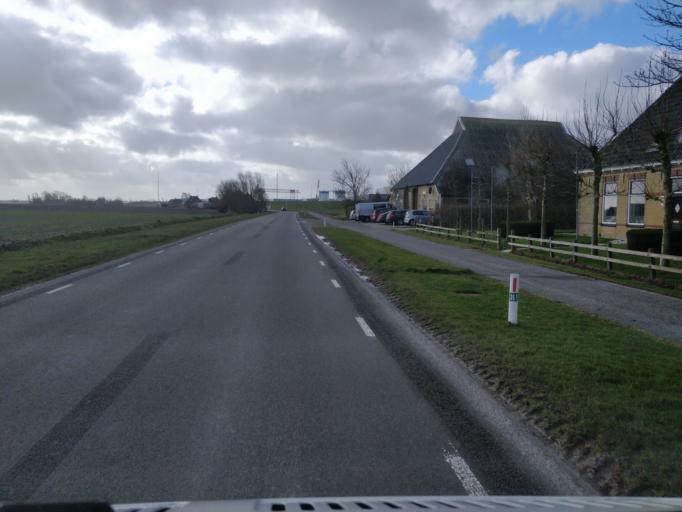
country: NL
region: Friesland
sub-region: Gemeente Harlingen
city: Harlingen
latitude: 53.1969
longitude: 5.4450
